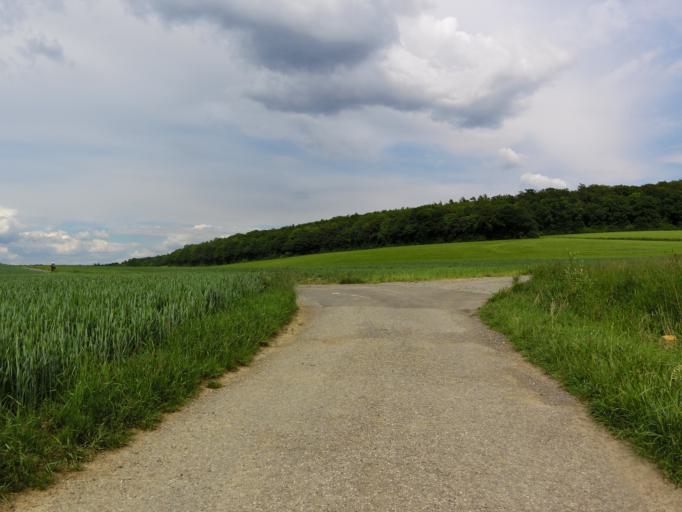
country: DE
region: Bavaria
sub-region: Regierungsbezirk Unterfranken
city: Kist
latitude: 49.7277
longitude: 9.8456
